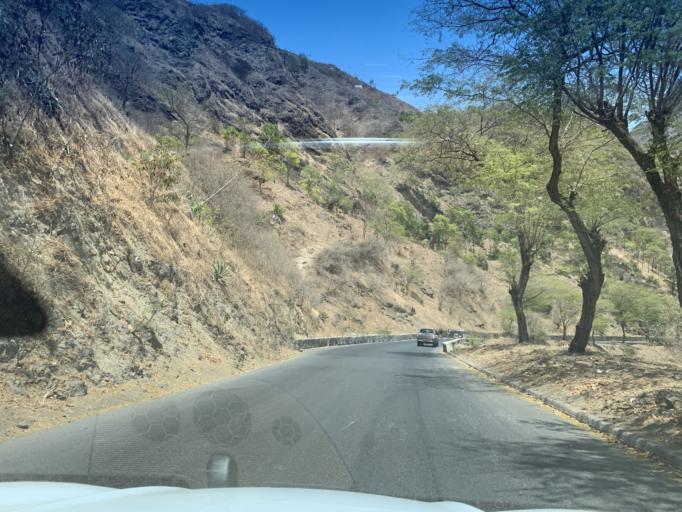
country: CV
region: Sao Salvador do Mundo
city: Picos
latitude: 15.0750
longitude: -23.6275
